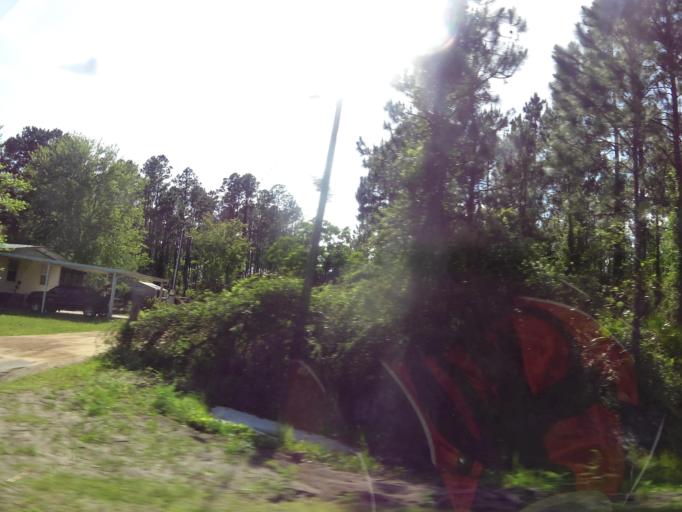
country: US
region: Florida
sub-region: Nassau County
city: Hilliard
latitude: 30.6513
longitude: -81.9032
